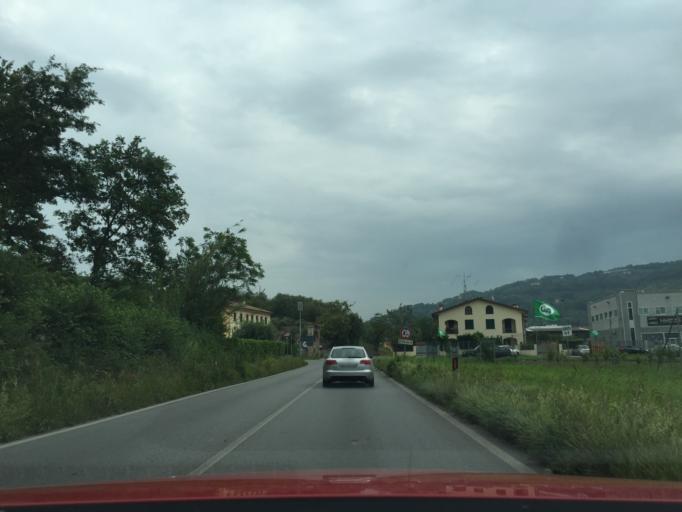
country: IT
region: Tuscany
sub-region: Provincia di Pistoia
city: Pieve a Nievole
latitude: 43.8893
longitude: 10.8148
